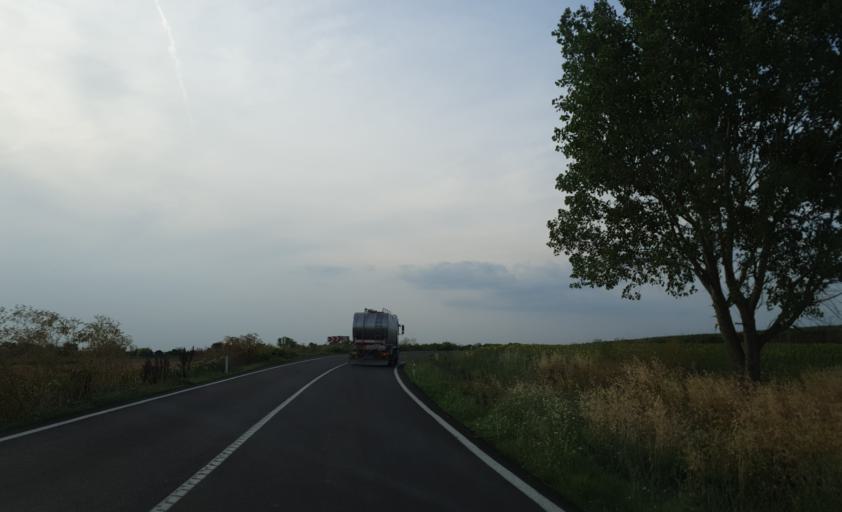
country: TR
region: Tekirdag
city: Hayrabolu
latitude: 41.2606
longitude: 27.1338
